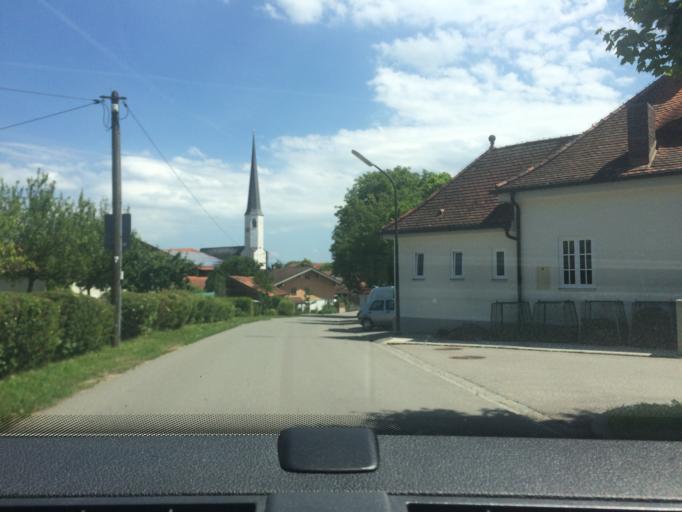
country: DE
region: Bavaria
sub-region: Upper Bavaria
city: Bruckmuhl
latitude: 47.8955
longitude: 11.9158
